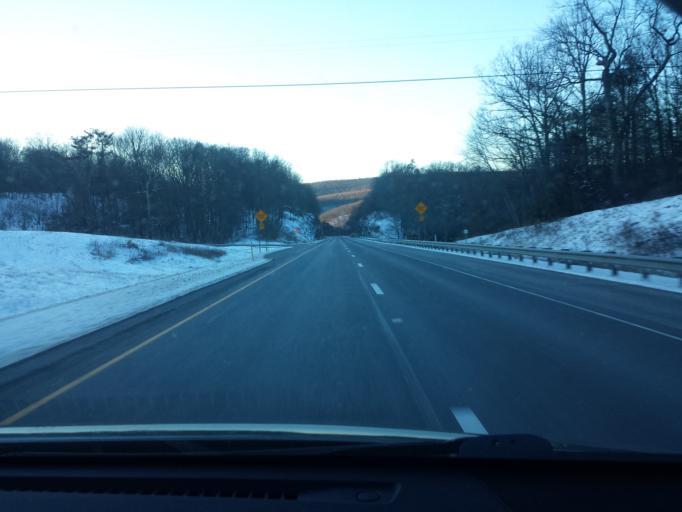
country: US
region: Pennsylvania
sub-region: Clinton County
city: Castanea
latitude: 41.0581
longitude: -77.3589
